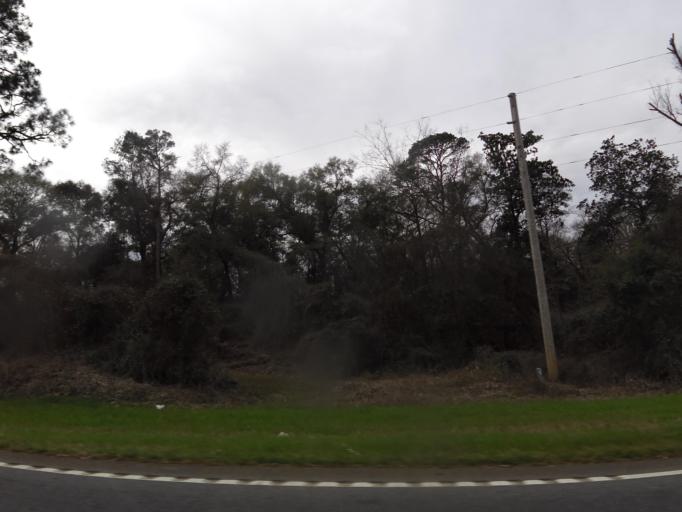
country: US
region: Georgia
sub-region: Randolph County
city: Shellman
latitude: 31.7782
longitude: -84.6041
